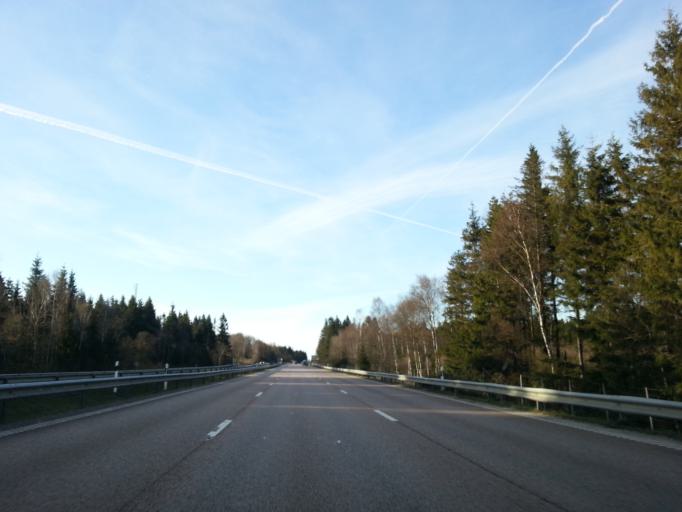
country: SE
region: Skane
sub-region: Bastads Kommun
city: Bastad
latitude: 56.3657
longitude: 12.9348
